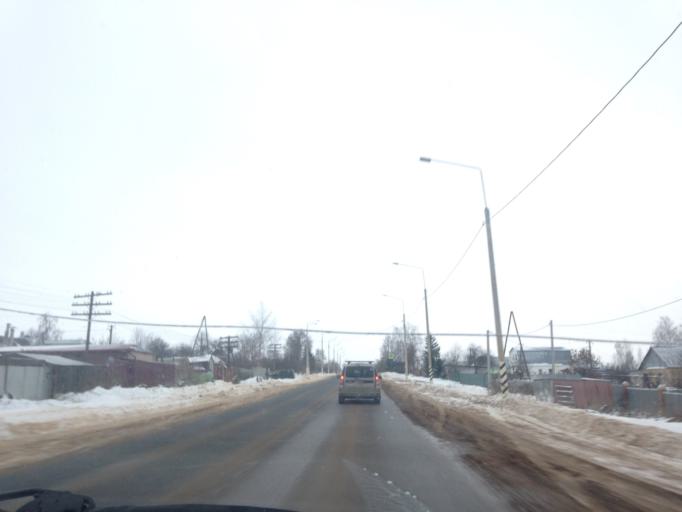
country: RU
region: Tula
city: Shchekino
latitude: 53.9914
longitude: 37.5064
